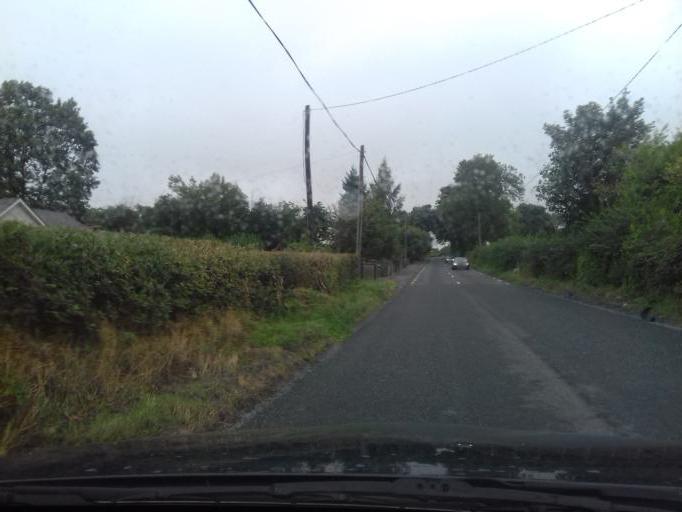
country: IE
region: Leinster
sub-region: Kilkenny
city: Graiguenamanagh
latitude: 52.6130
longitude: -6.9369
